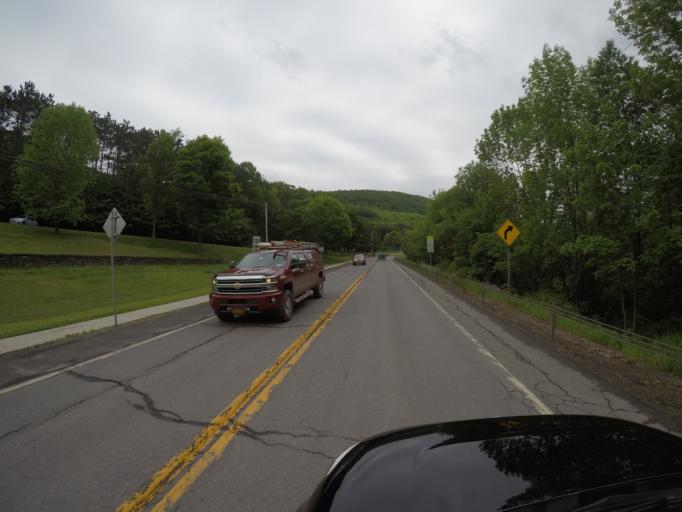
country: US
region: New York
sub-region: Delaware County
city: Delhi
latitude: 42.2709
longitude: -74.9161
